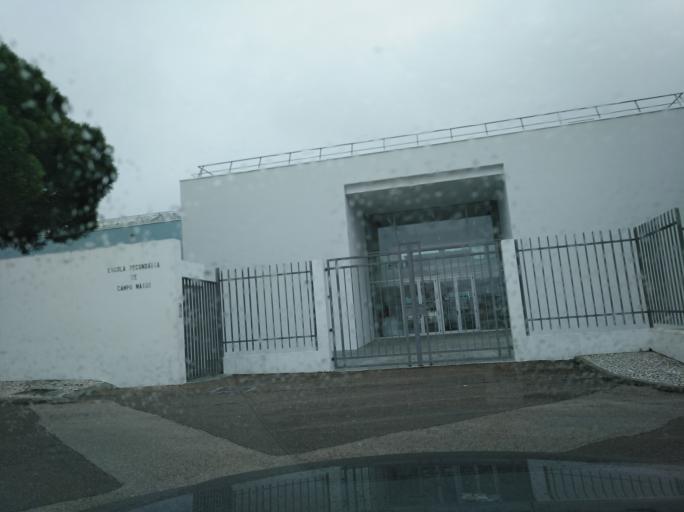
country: PT
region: Portalegre
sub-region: Campo Maior
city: Campo Maior
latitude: 39.0183
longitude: -7.0653
